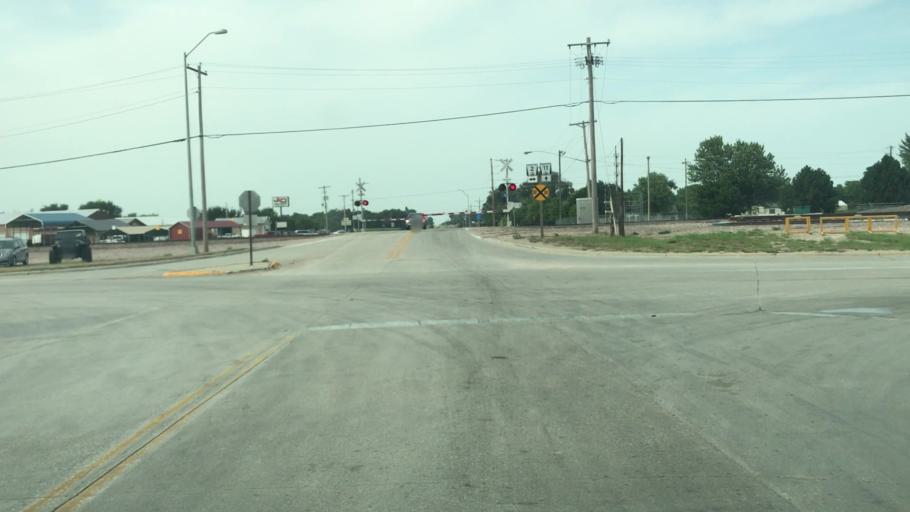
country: US
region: Nebraska
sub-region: Hall County
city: Wood River
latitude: 41.0018
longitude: -98.6074
